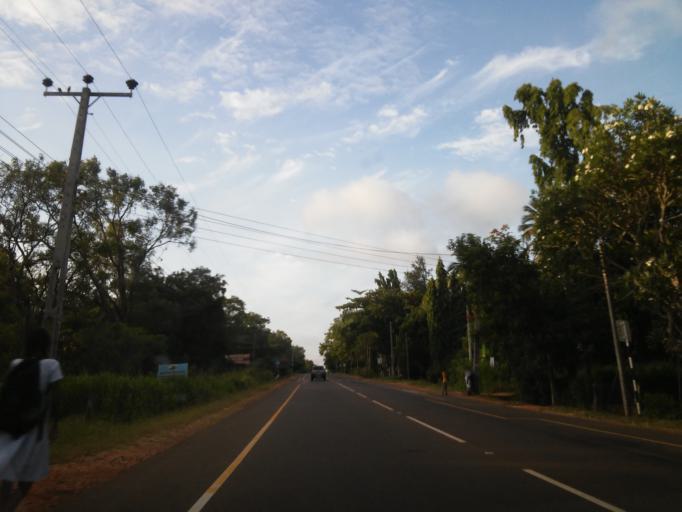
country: LK
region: North Central
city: Anuradhapura
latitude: 8.1581
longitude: 80.5401
